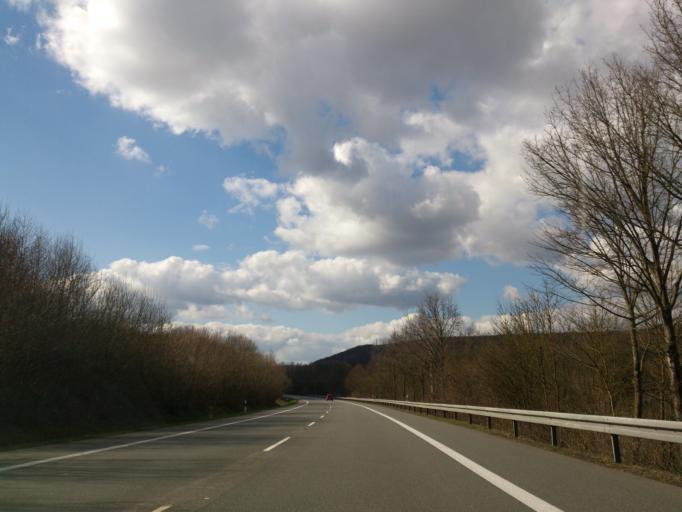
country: DE
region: North Rhine-Westphalia
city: Brakel
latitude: 51.7014
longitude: 9.1455
